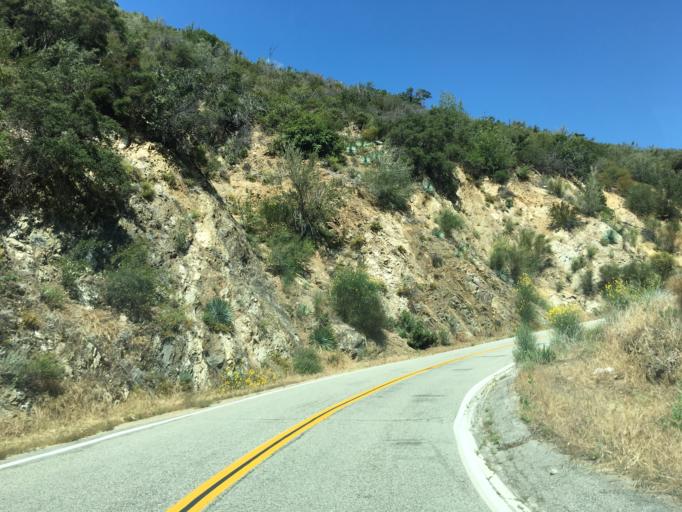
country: US
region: California
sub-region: Los Angeles County
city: Glendora
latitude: 34.2189
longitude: -117.7930
